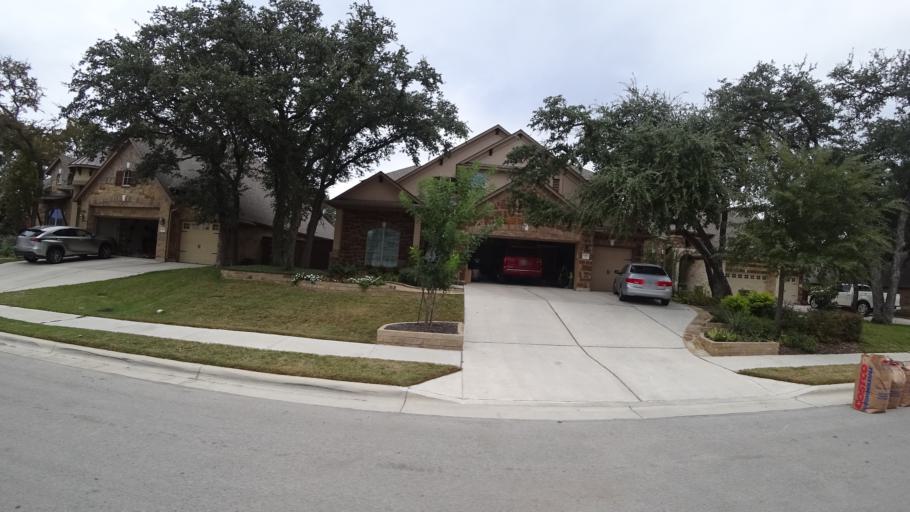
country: US
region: Texas
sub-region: Travis County
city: Manchaca
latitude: 30.1414
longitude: -97.8512
